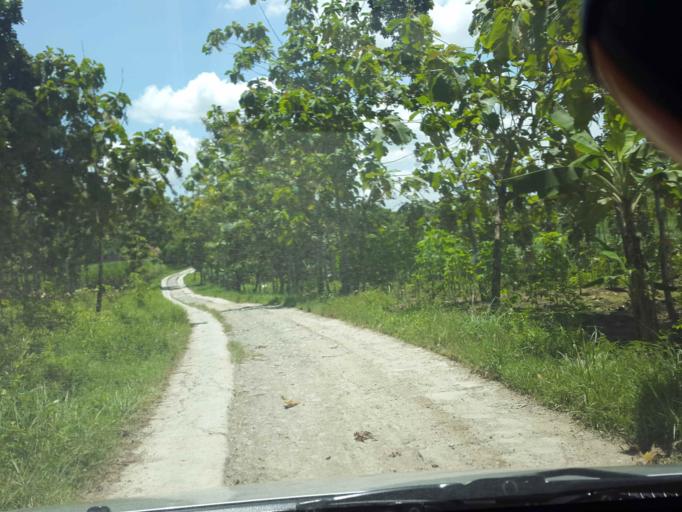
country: ID
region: Central Java
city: Sragen
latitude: -7.2716
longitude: 111.1312
